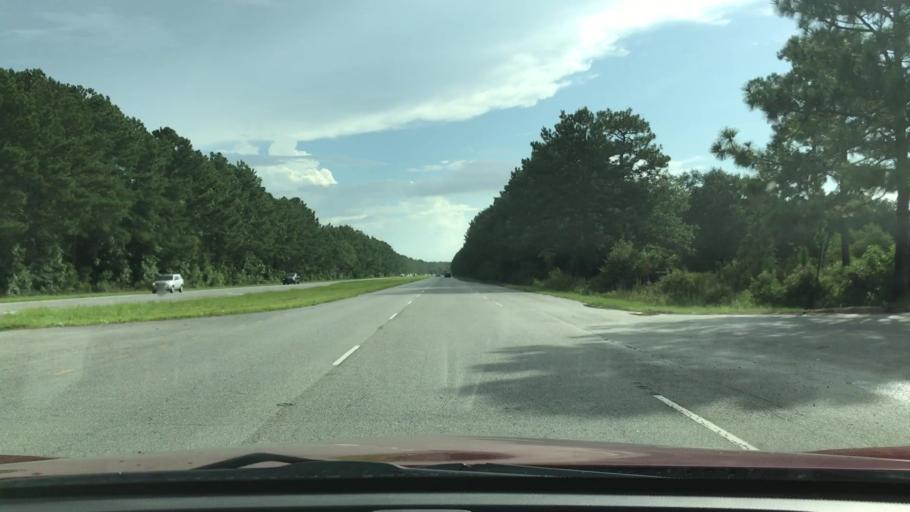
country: US
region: South Carolina
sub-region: Charleston County
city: Awendaw
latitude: 32.9751
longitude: -79.6695
